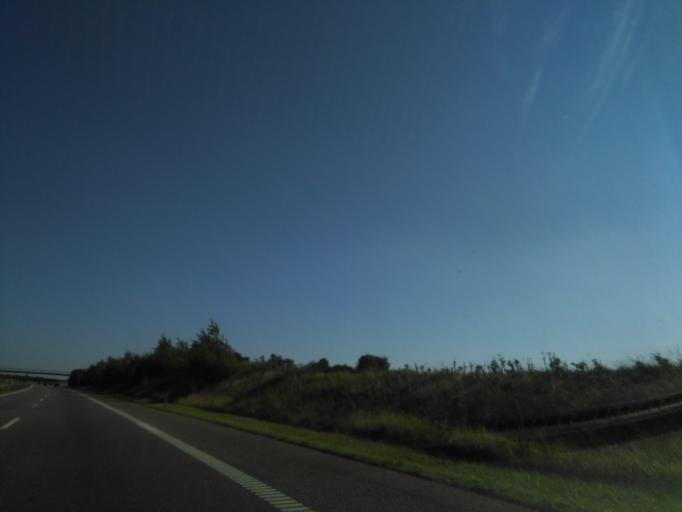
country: DK
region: Central Jutland
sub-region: Arhus Kommune
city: Lystrup
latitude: 56.2284
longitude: 10.2561
